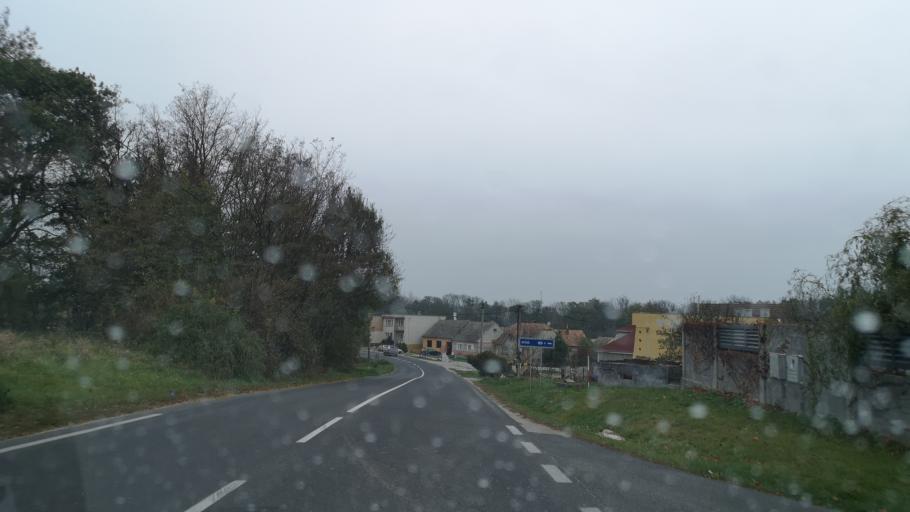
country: SK
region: Trnavsky
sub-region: Okres Trnava
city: Trnava
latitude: 48.5160
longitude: 17.6114
